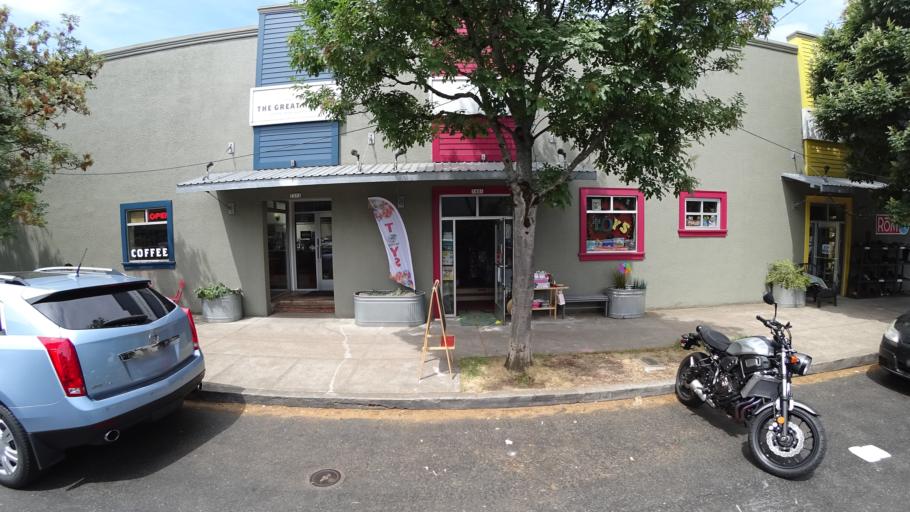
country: US
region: Oregon
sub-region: Washington County
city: West Haven
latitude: 45.5905
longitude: -122.7546
